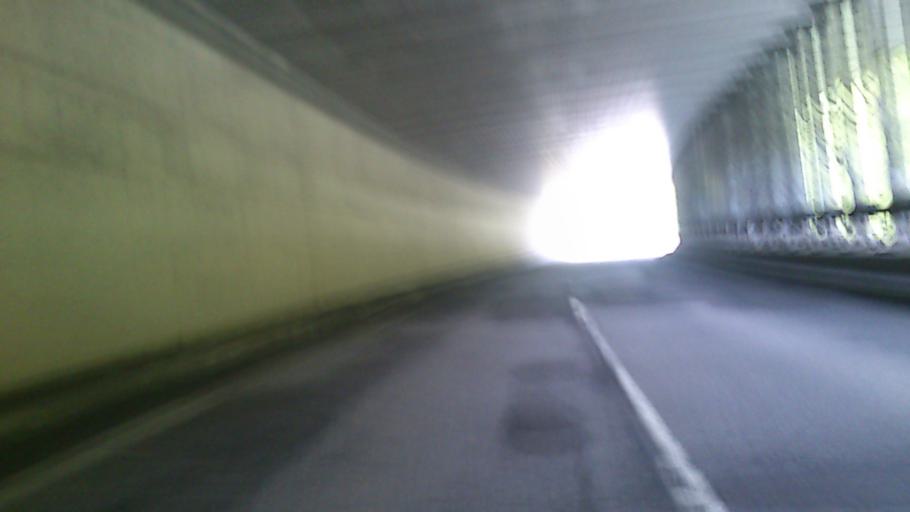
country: JP
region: Hokkaido
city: Kamikawa
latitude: 43.7479
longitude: 142.9341
